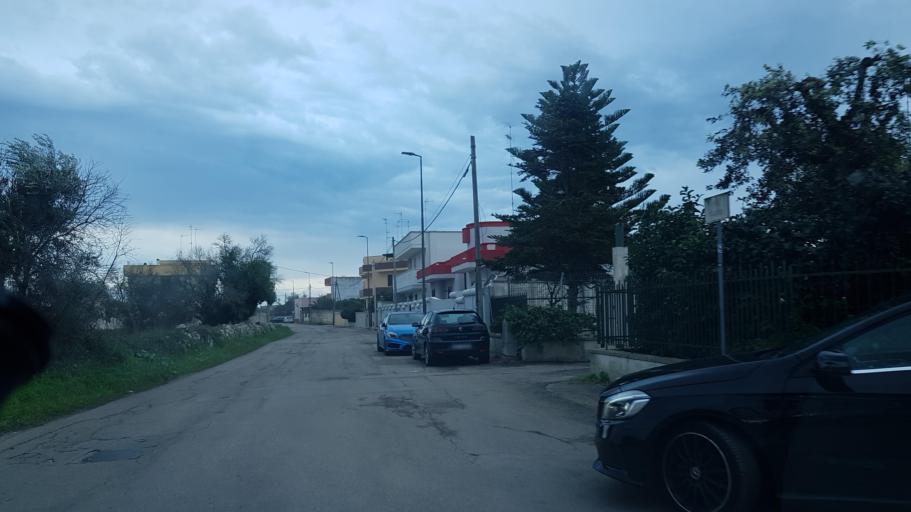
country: IT
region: Apulia
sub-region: Provincia di Lecce
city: Merine
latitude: 40.3288
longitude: 18.2230
